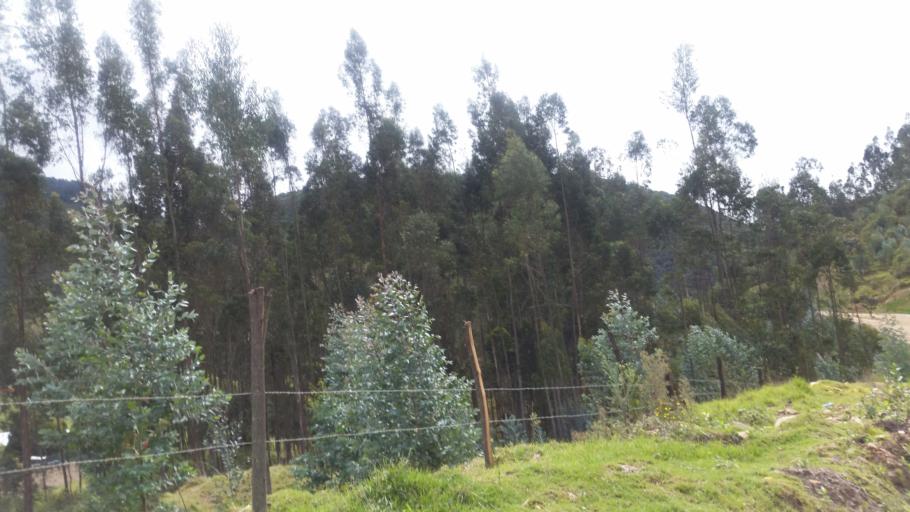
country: CO
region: Cundinamarca
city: La Calera
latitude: 4.7232
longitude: -73.9535
